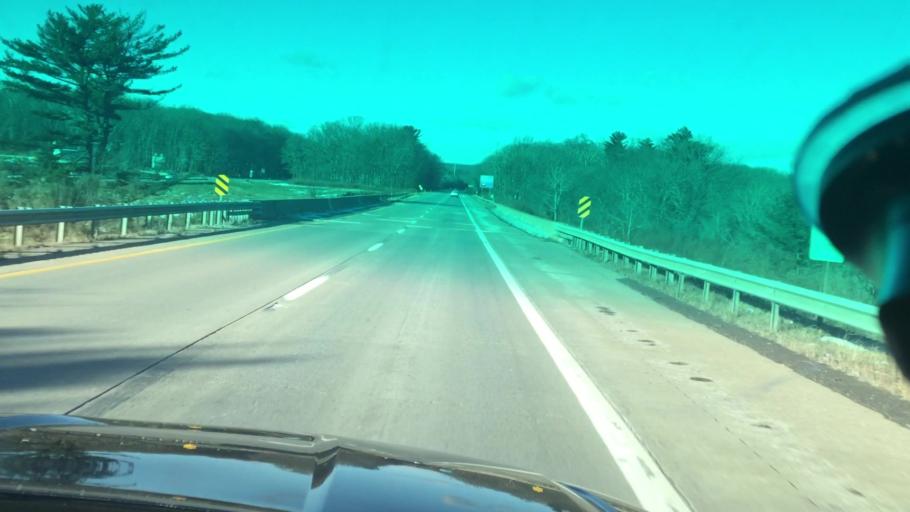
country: US
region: Pennsylvania
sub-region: Luzerne County
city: Nanticoke
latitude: 41.1346
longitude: -75.9624
